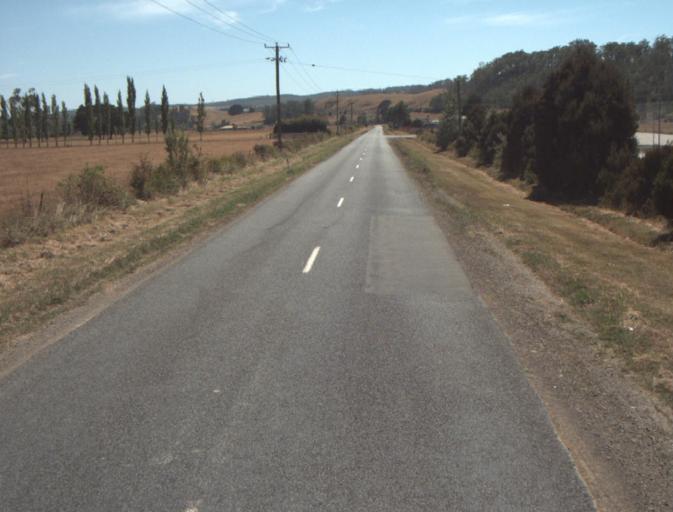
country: AU
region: Tasmania
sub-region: Launceston
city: Mayfield
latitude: -41.2545
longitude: 147.1468
